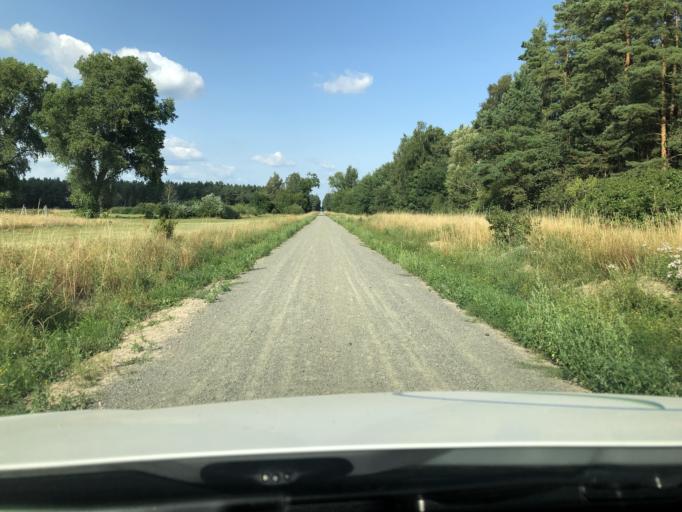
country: SE
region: Skane
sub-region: Kristianstads Kommun
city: Norra Asum
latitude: 55.9114
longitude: 14.1133
